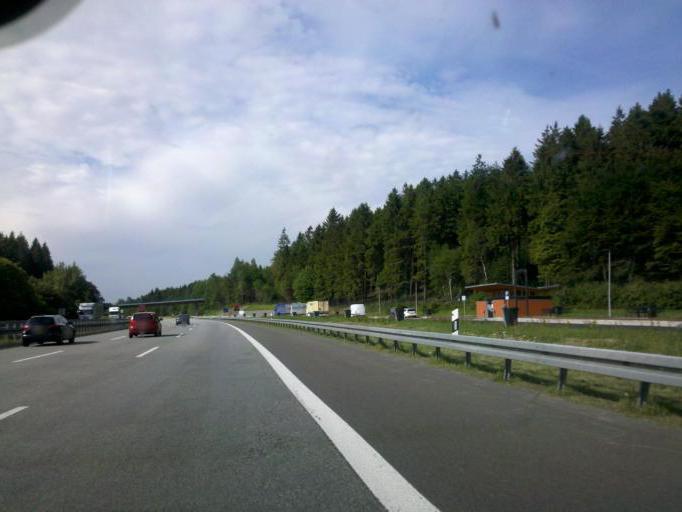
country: DE
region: North Rhine-Westphalia
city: Meinerzhagen
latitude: 51.1221
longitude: 7.6679
